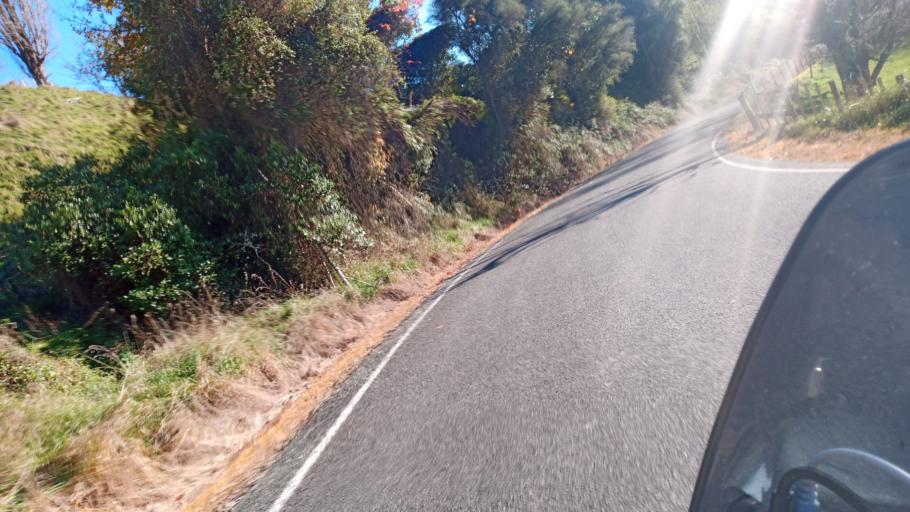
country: NZ
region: Hawke's Bay
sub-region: Wairoa District
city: Wairoa
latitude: -38.8202
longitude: 177.2952
